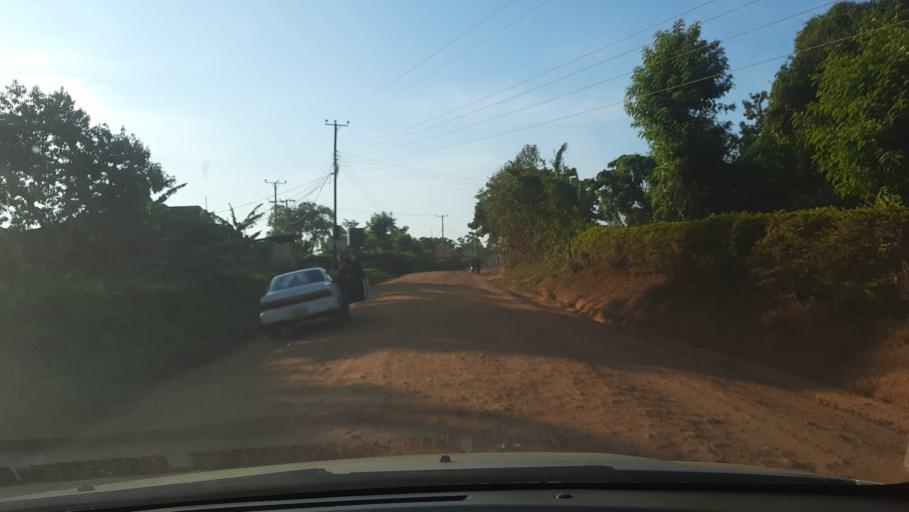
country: UG
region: Central Region
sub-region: Mukono District
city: Mukono
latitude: 0.3725
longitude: 32.7486
